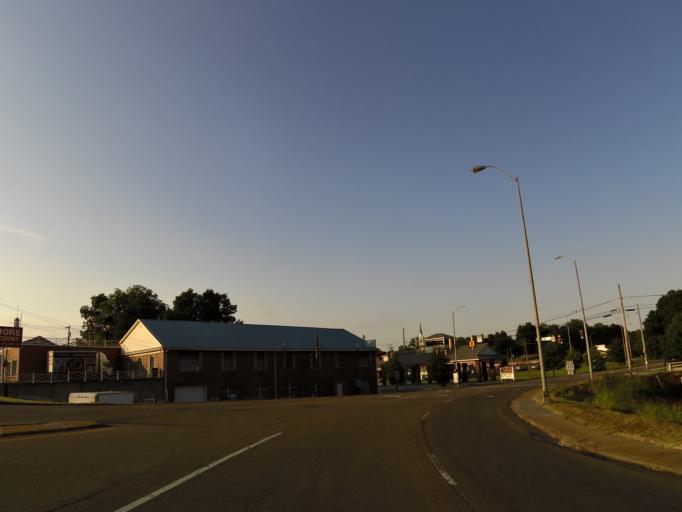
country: US
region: Tennessee
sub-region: McMinn County
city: Athens
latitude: 35.4406
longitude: -84.5924
